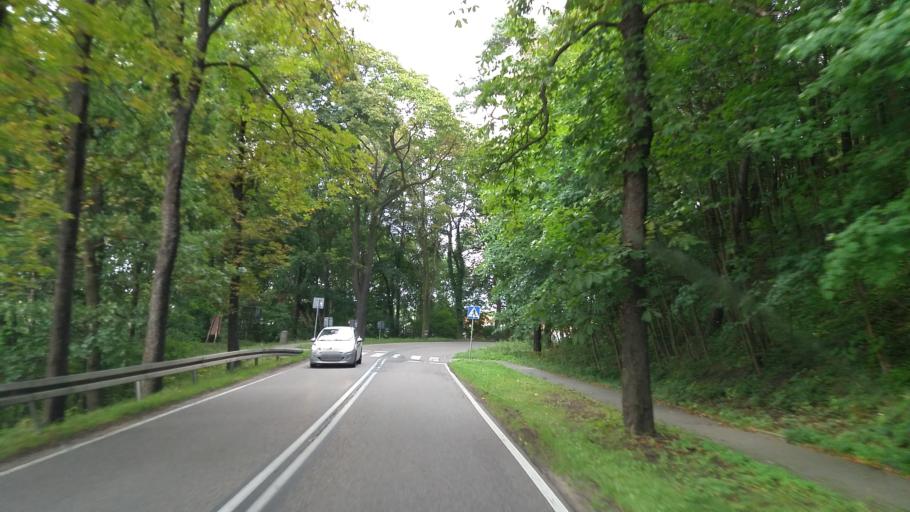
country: PL
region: West Pomeranian Voivodeship
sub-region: Powiat mysliborski
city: Barlinek
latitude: 53.0013
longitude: 15.2249
